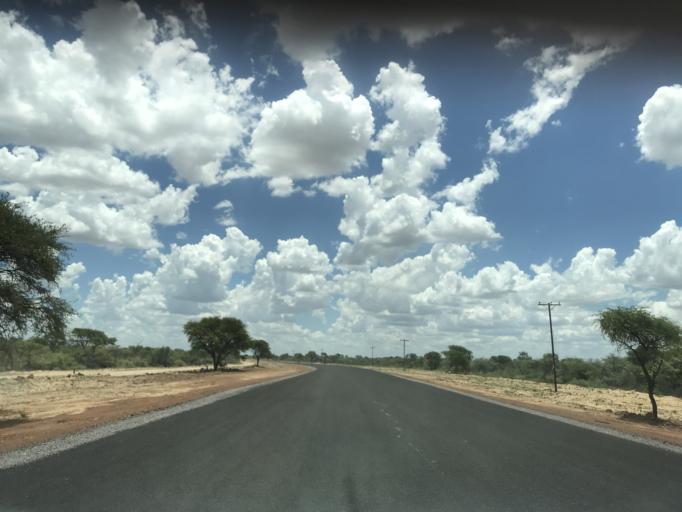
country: BW
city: Mabuli
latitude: -25.7985
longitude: 24.6686
